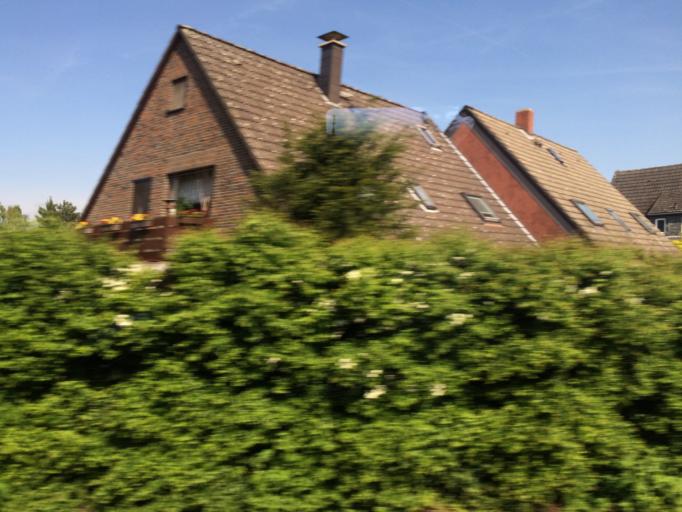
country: DE
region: North Rhine-Westphalia
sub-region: Regierungsbezirk Dusseldorf
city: Ratingen
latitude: 51.3245
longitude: 6.7828
